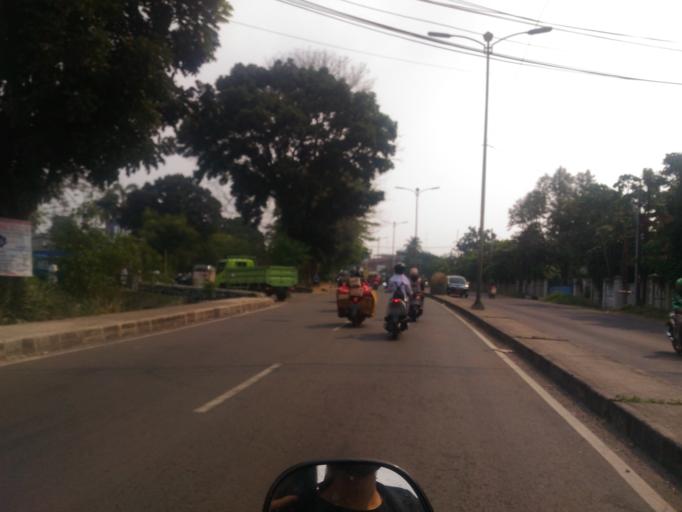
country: ID
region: West Java
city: Cibinong
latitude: -6.5266
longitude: 106.8315
